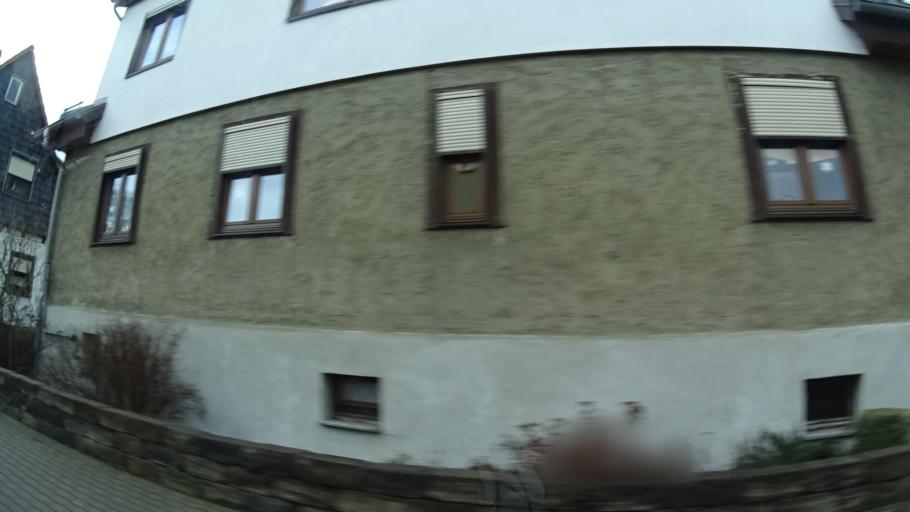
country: DE
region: Thuringia
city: Kaltenwestheim
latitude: 50.6095
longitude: 10.1172
